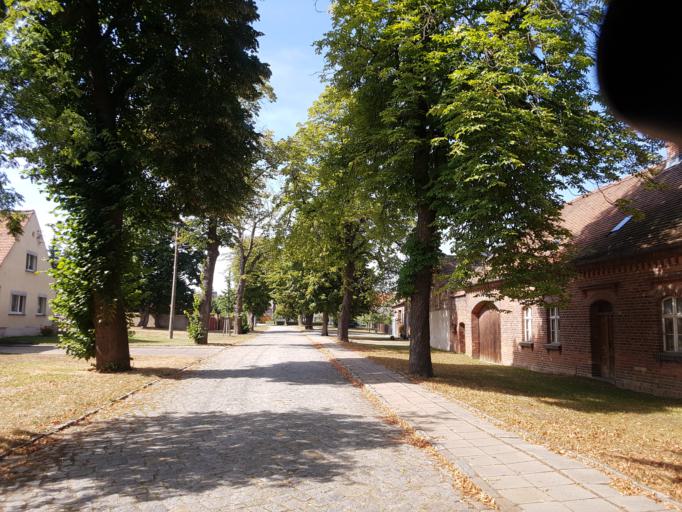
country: DE
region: Brandenburg
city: Drahnsdorf
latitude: 51.8539
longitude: 13.6107
